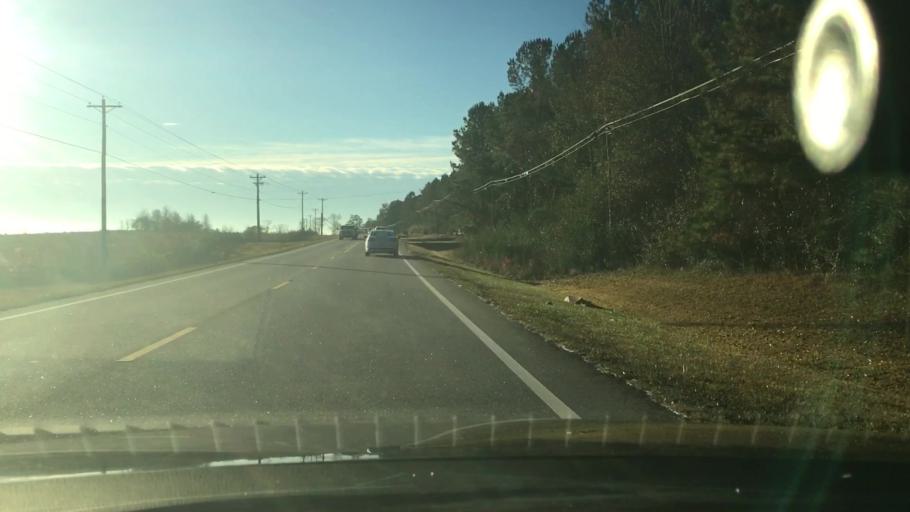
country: US
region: Georgia
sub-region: Coweta County
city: Senoia
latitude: 33.2804
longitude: -84.5356
